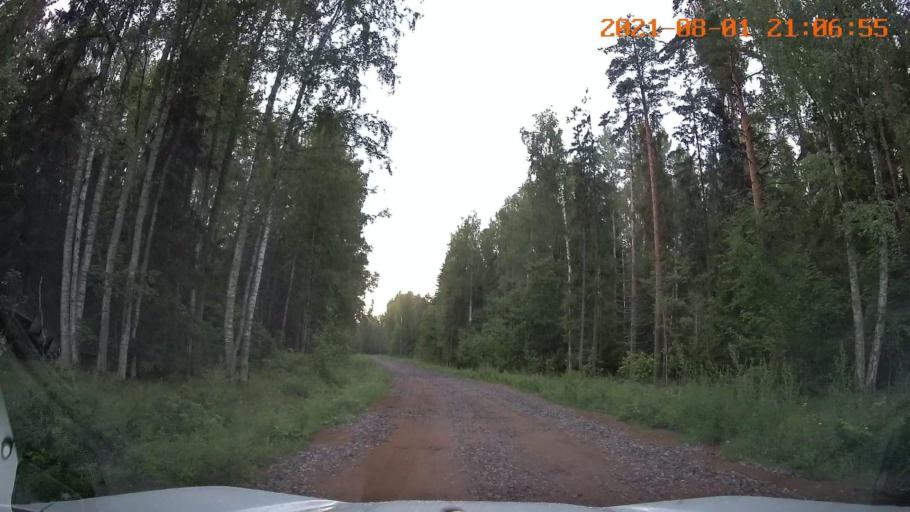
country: RU
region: Leningrad
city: Syas'stroy
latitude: 60.5029
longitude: 32.6495
